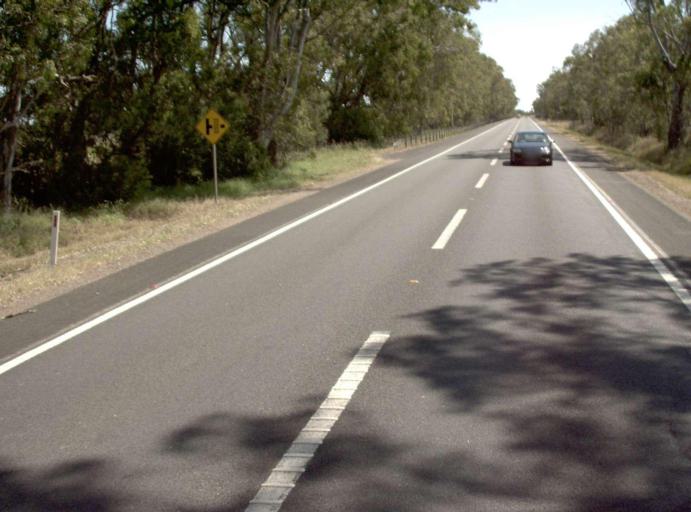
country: AU
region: Victoria
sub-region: Wellington
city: Sale
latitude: -37.9531
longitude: 147.1064
